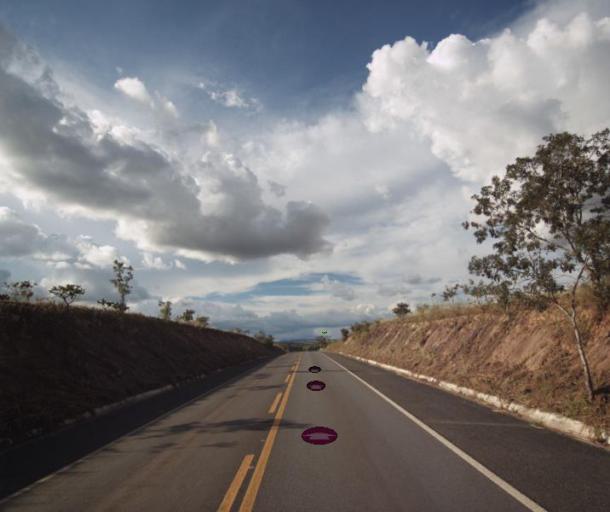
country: BR
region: Goias
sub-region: Barro Alto
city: Barro Alto
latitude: -14.7955
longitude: -48.6327
